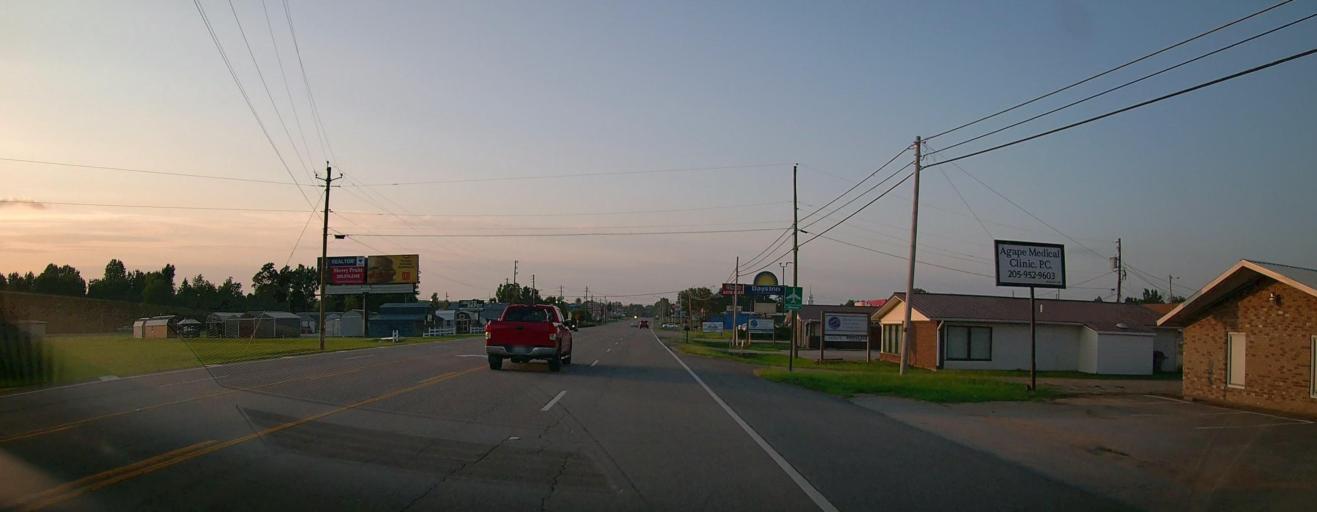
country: US
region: Alabama
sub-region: Marion County
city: Hamilton
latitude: 34.1166
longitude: -87.9894
